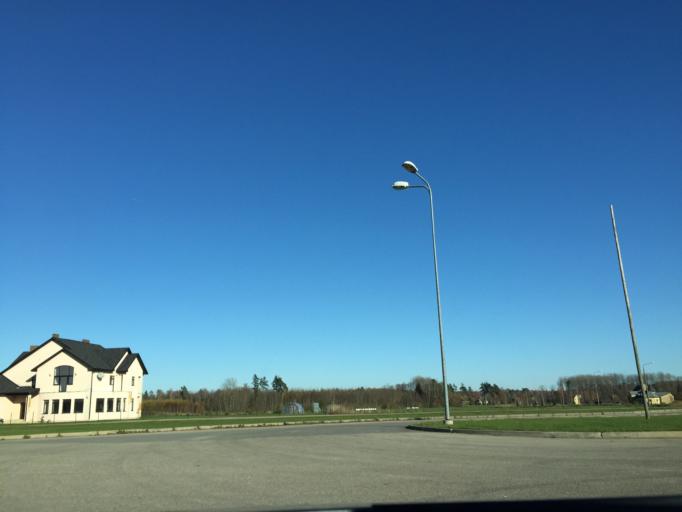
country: LV
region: Aizkraukles Rajons
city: Aizkraukle
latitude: 56.6101
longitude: 25.2606
